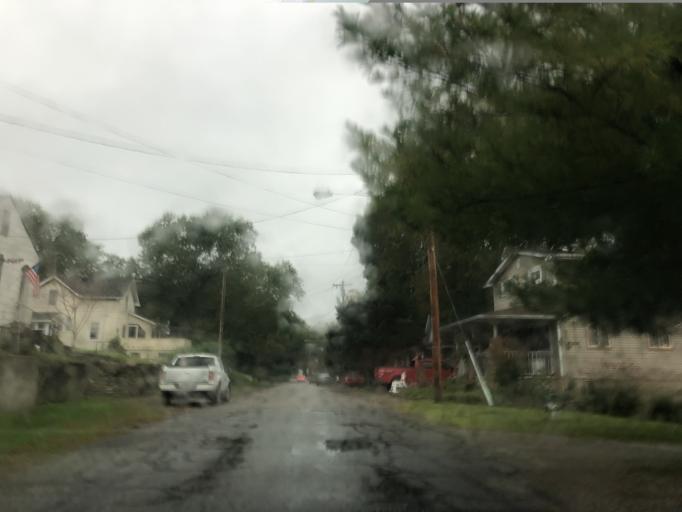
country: US
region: Ohio
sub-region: Hamilton County
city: Loveland
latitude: 39.2712
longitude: -84.2612
